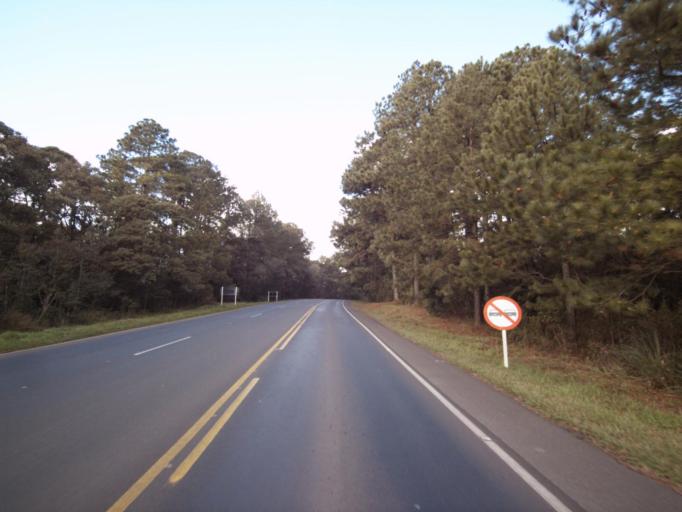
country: BR
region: Santa Catarina
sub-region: Concordia
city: Concordia
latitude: -26.9796
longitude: -51.7986
